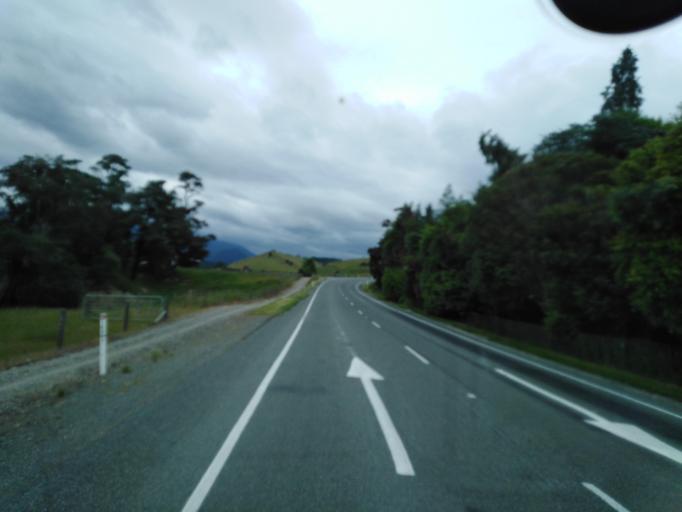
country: NZ
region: Tasman
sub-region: Tasman District
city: Wakefield
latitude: -41.4601
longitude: 172.9523
